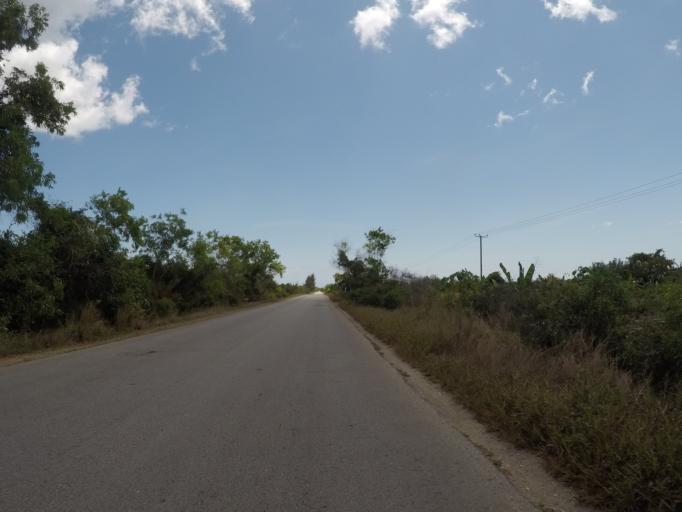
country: TZ
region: Zanzibar Central/South
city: Nganane
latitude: -6.2835
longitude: 39.4646
